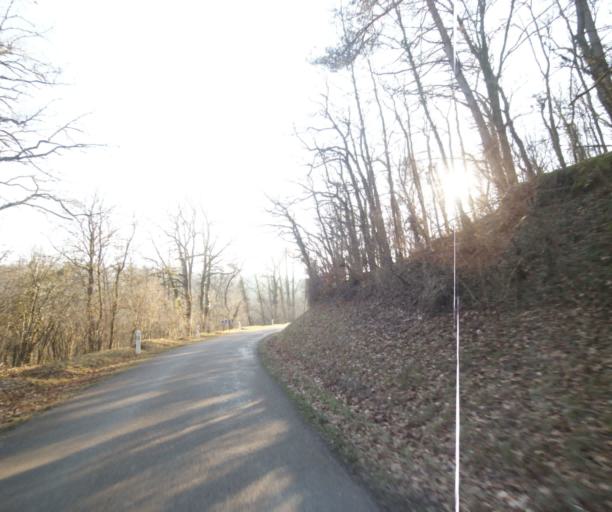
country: FR
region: Champagne-Ardenne
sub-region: Departement de la Haute-Marne
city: Chevillon
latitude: 48.5458
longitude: 5.1235
